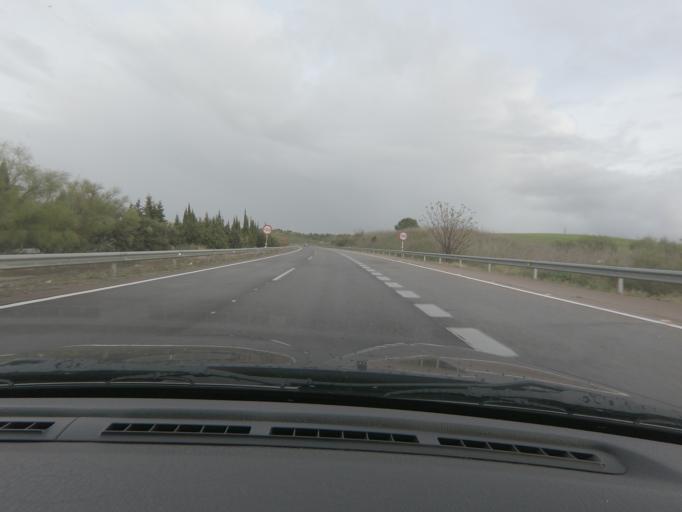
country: ES
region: Extremadura
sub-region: Provincia de Badajoz
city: Badajoz
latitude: 38.8871
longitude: -6.9120
